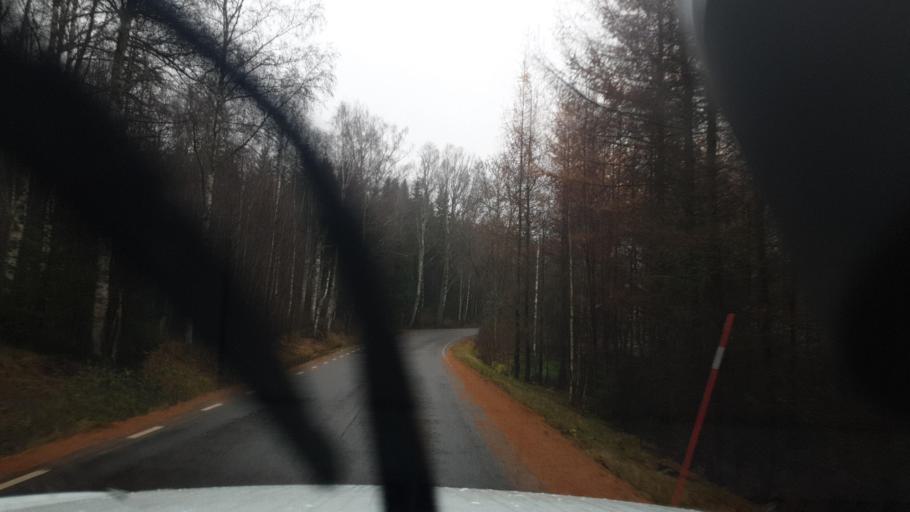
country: SE
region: Vaermland
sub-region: Arvika Kommun
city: Arvika
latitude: 59.6529
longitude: 12.8075
